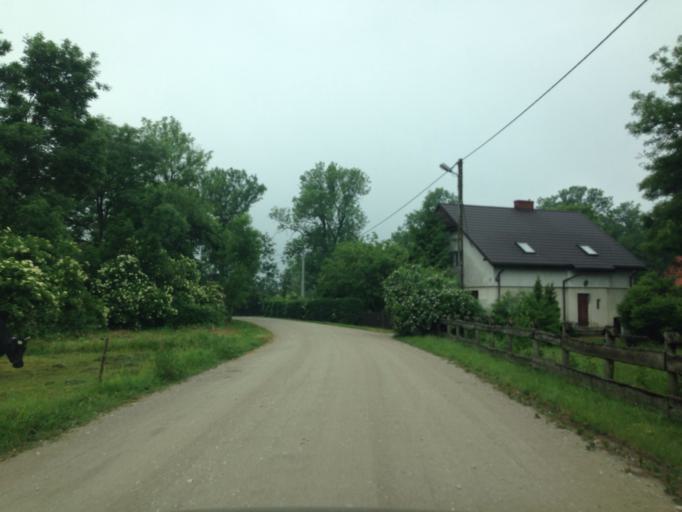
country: PL
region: Kujawsko-Pomorskie
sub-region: Powiat brodnicki
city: Bobrowo
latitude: 53.3429
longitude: 19.3046
